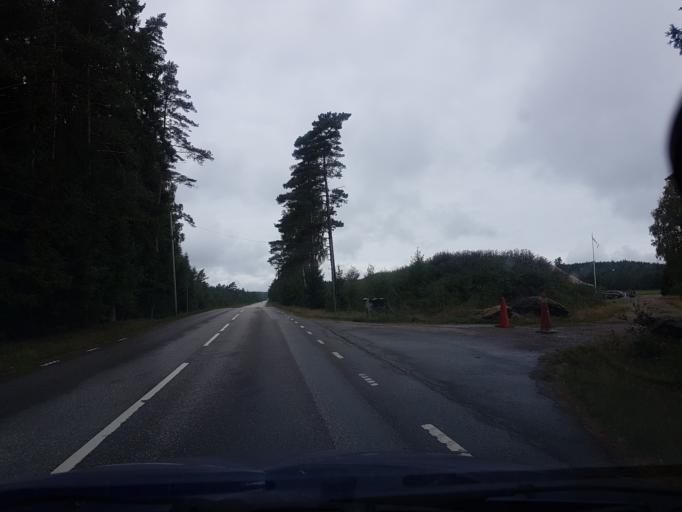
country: SE
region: Vaestra Goetaland
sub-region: Lerums Kommun
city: Grabo
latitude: 57.9203
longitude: 12.3053
